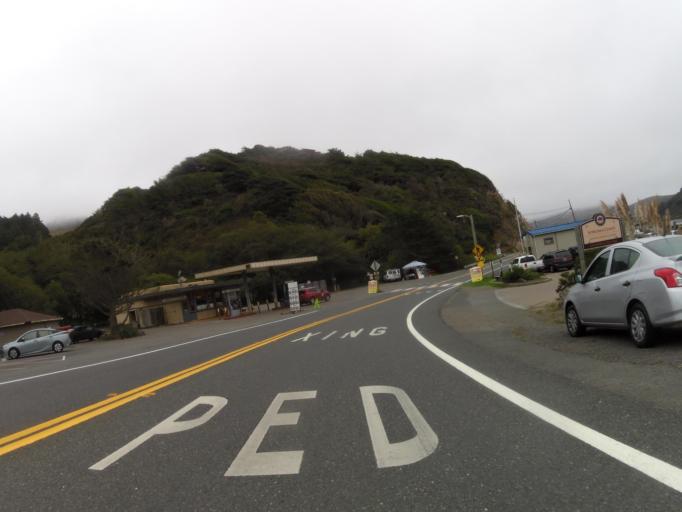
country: US
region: California
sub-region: Sonoma County
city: Monte Rio
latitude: 38.4497
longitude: -123.1152
